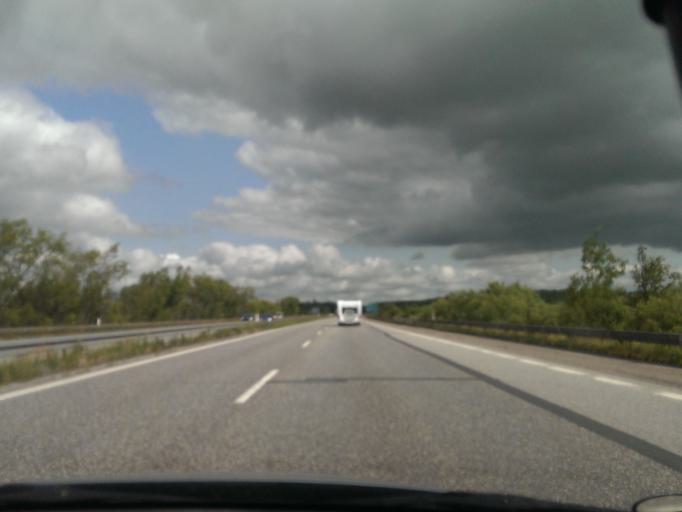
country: DK
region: North Denmark
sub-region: Mariagerfjord Kommune
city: Hobro
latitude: 56.6291
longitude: 9.7338
